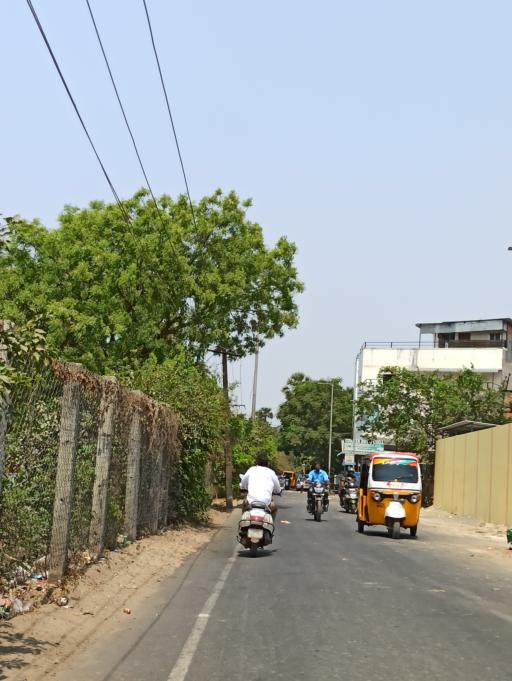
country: IN
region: Tamil Nadu
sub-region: Thiruvallur
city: Chinnasekkadu
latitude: 13.1513
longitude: 80.2435
